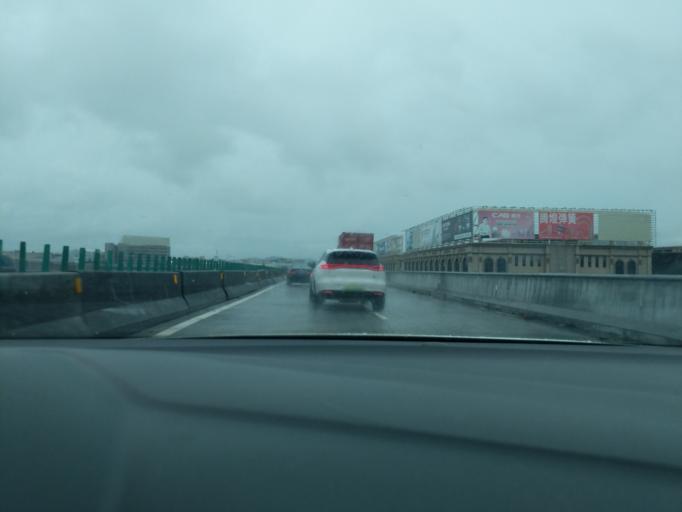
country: CN
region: Guangdong
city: Shuikou
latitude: 22.4765
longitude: 112.7673
